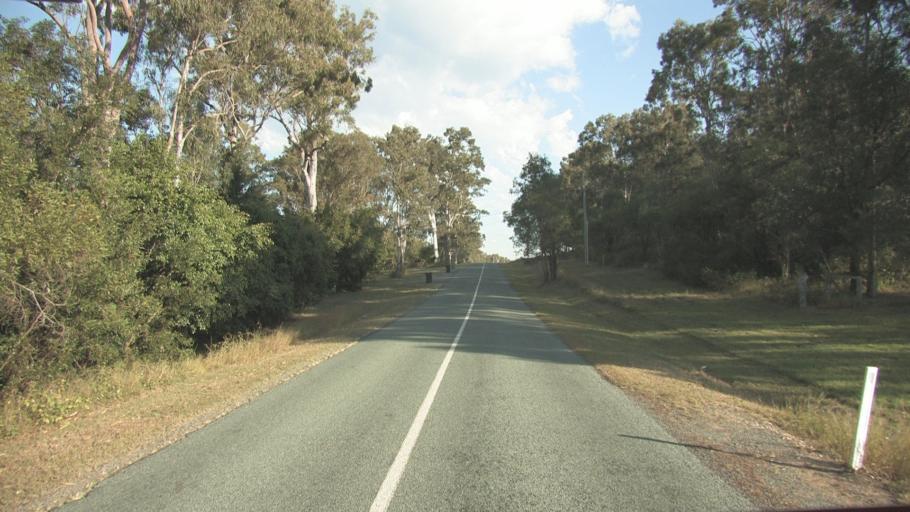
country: AU
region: Queensland
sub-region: Gold Coast
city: Ormeau Hills
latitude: -27.8332
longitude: 153.1698
